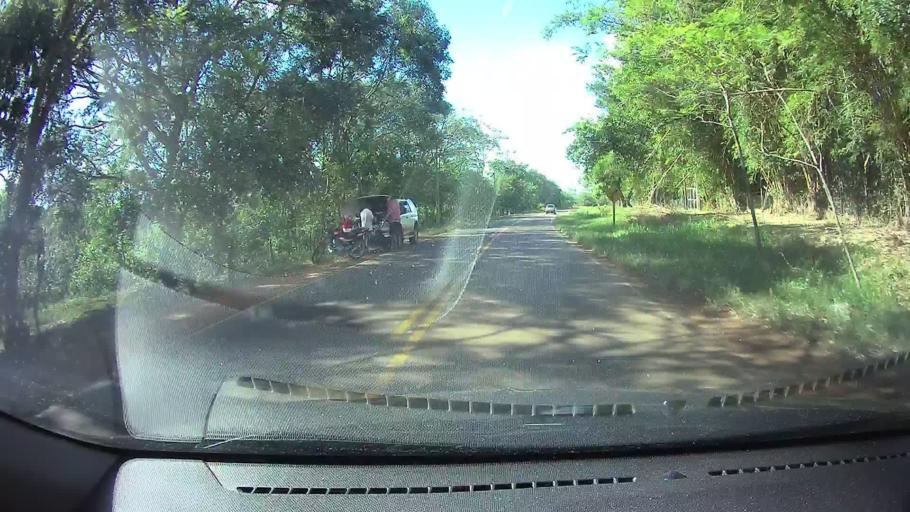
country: PY
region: Cordillera
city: Itacurubi de la Cordillera
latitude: -25.4766
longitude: -56.8812
